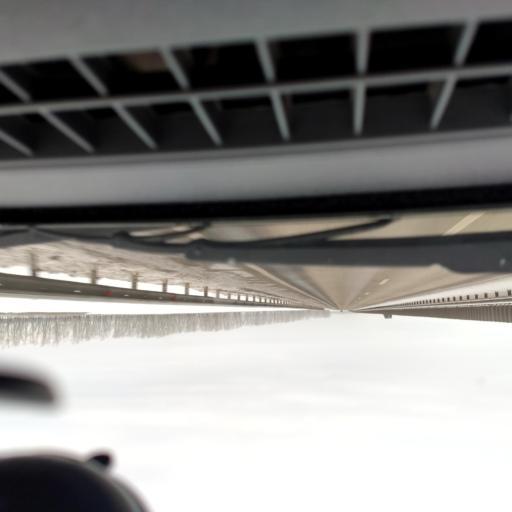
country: RU
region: Bashkortostan
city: Kushnarenkovo
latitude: 55.0912
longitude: 55.2508
